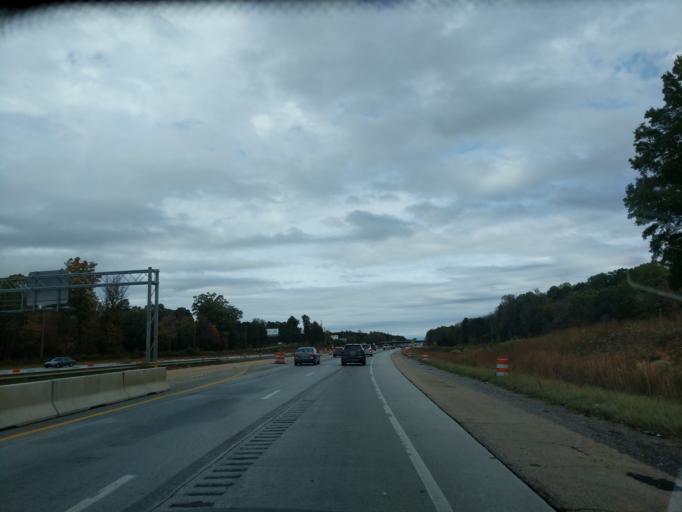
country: US
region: North Carolina
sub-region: Rowan County
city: China Grove
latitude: 35.5822
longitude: -80.5518
